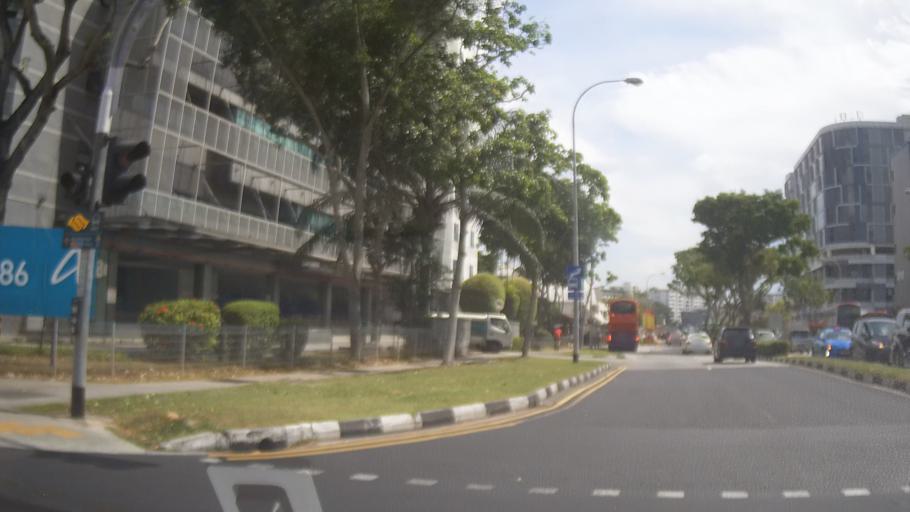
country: SG
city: Singapore
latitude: 1.3274
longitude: 103.8931
